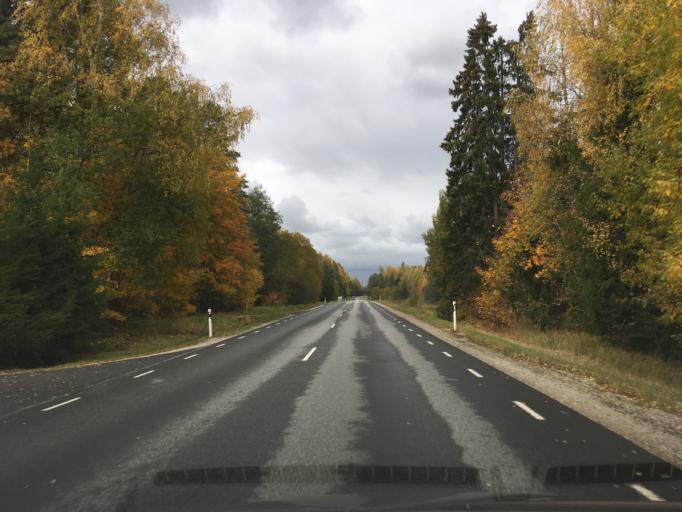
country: EE
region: Harju
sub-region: Anija vald
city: Kehra
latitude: 59.2955
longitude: 25.3717
